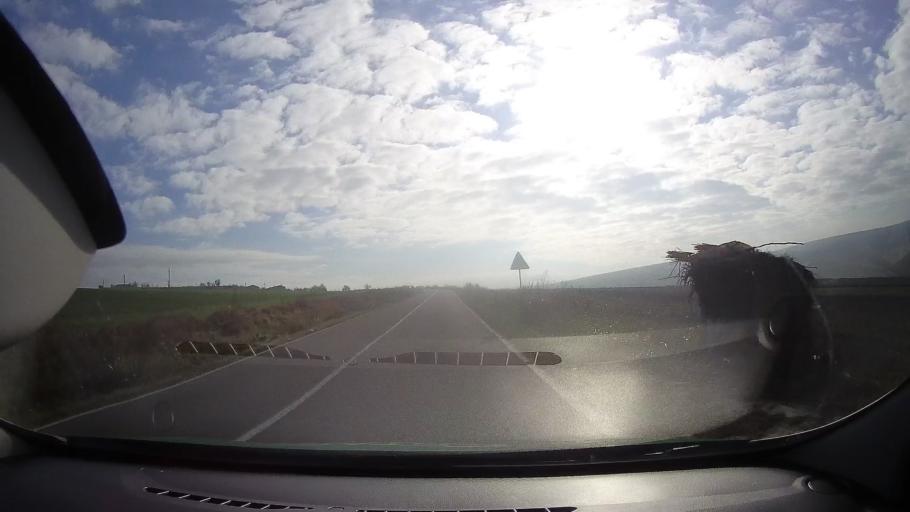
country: RO
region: Tulcea
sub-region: Comuna Bestepe
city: Bestepe
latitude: 45.0832
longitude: 29.0229
